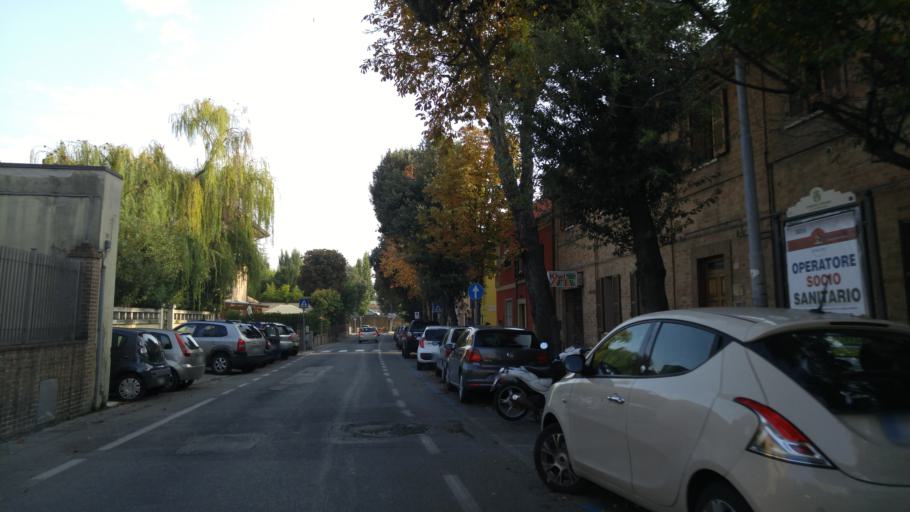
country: IT
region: The Marches
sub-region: Provincia di Pesaro e Urbino
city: Pesaro
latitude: 43.9069
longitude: 12.9172
